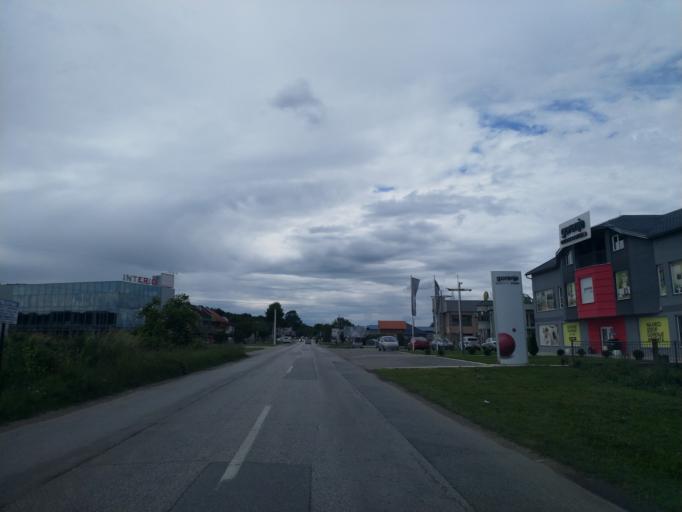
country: RS
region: Central Serbia
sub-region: Pomoravski Okrug
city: Jagodina
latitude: 43.9603
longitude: 21.2844
